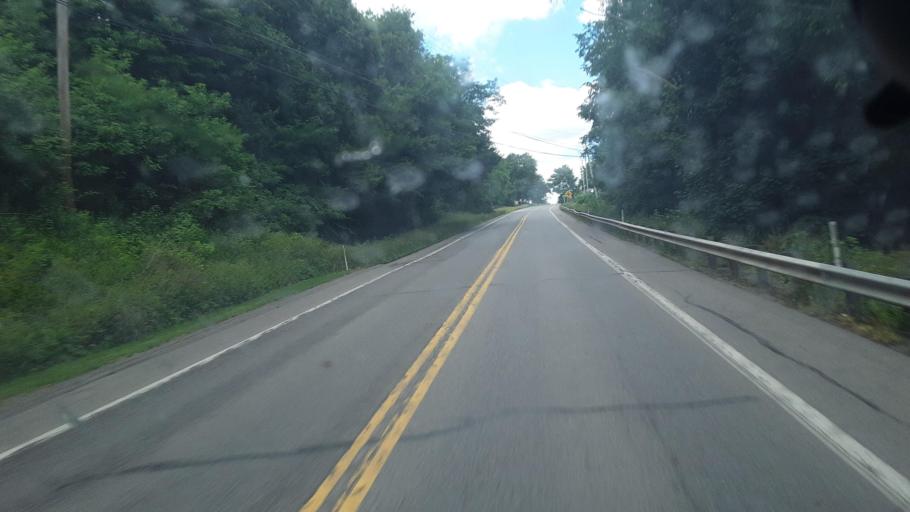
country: US
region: Pennsylvania
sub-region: Butler County
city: Slippery Rock
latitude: 40.9858
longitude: -80.1709
